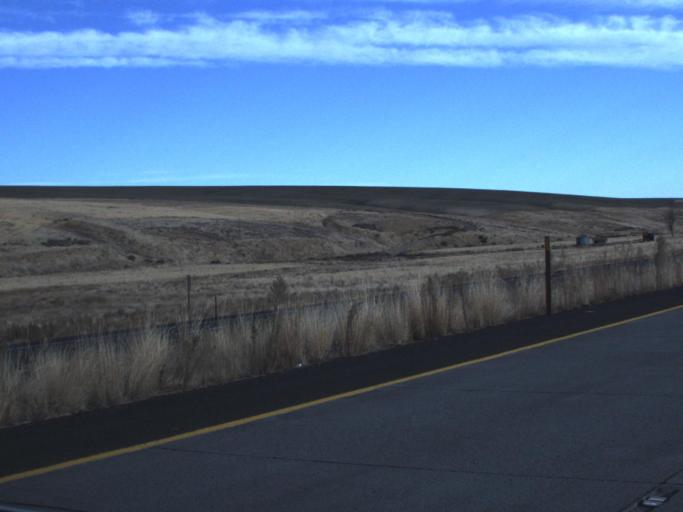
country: US
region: Washington
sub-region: Franklin County
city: Connell
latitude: 46.8484
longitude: -118.6413
